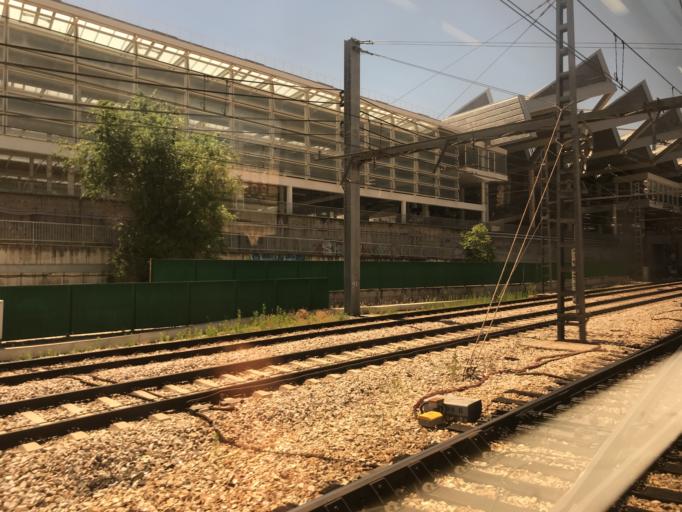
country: ES
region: Madrid
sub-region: Provincia de Madrid
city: Retiro
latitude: 40.4035
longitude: -3.6859
